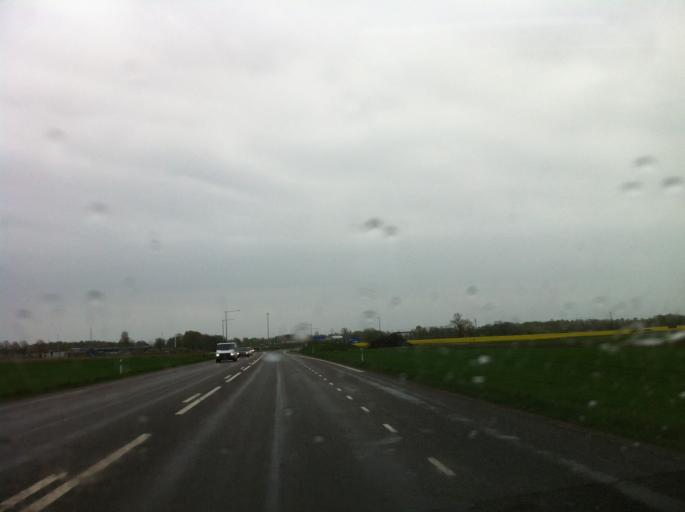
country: SE
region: Halland
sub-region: Falkenbergs Kommun
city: Falkenberg
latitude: 56.9256
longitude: 12.5099
